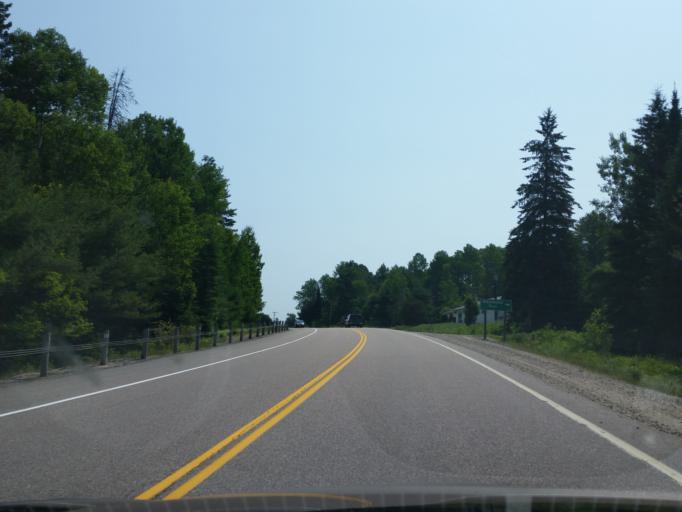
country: CA
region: Ontario
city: Deep River
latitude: 46.1716
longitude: -77.7040
